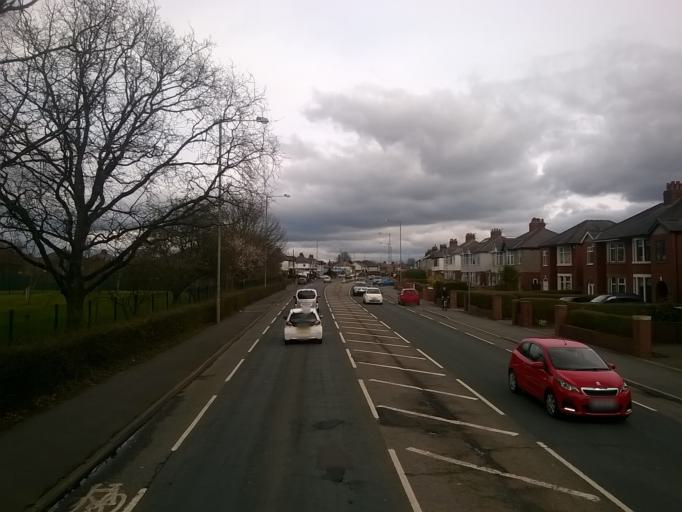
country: GB
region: England
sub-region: Lancashire
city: Preston
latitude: 53.7689
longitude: -2.7493
